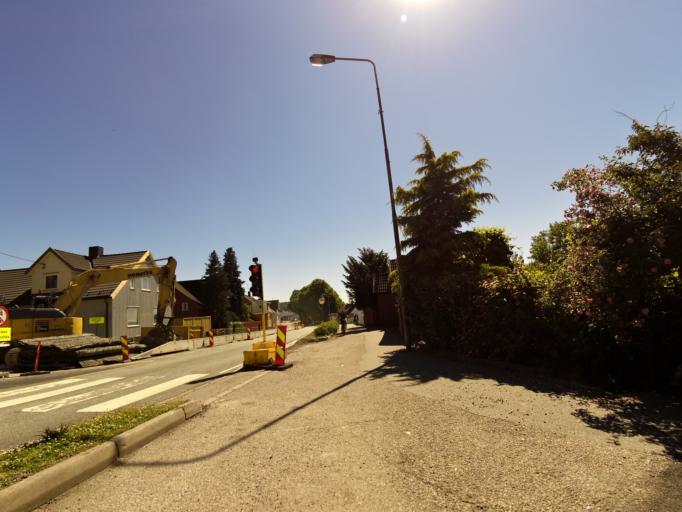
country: NO
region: Vest-Agder
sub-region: Kristiansand
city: Kristiansand
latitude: 58.1542
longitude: 8.0092
